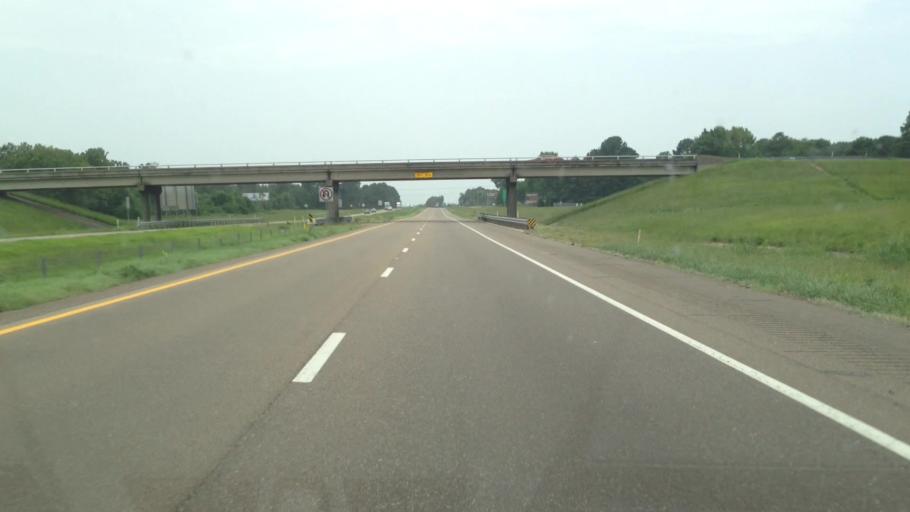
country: US
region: Texas
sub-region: Bowie County
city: New Boston
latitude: 33.4758
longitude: -94.4238
